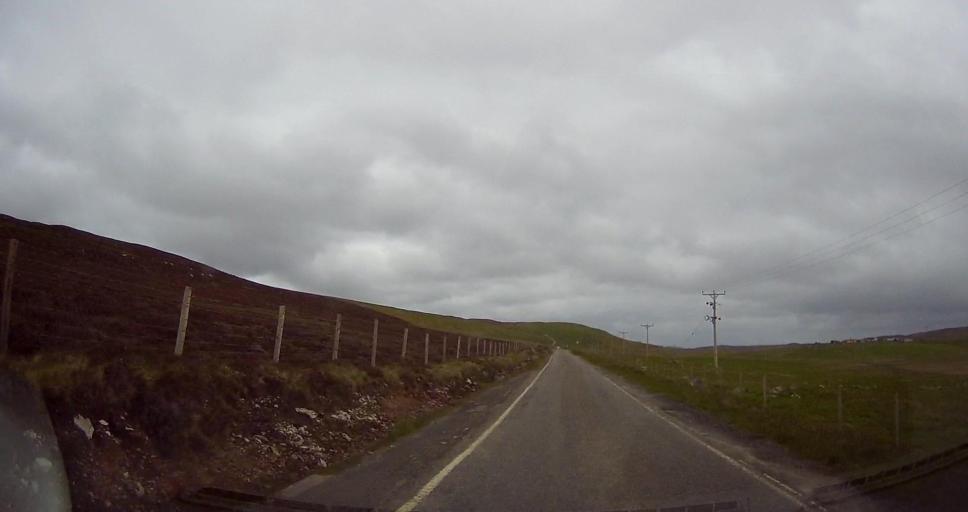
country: GB
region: Scotland
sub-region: Shetland Islands
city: Sandwick
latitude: 60.2443
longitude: -1.5119
